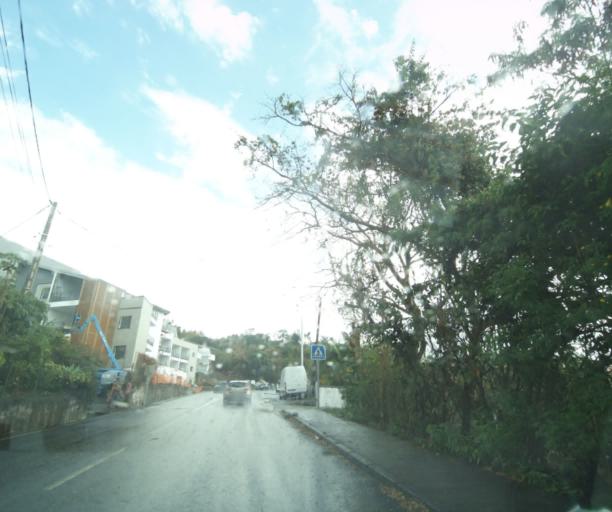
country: RE
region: Reunion
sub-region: Reunion
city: La Possession
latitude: -20.9844
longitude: 55.3339
